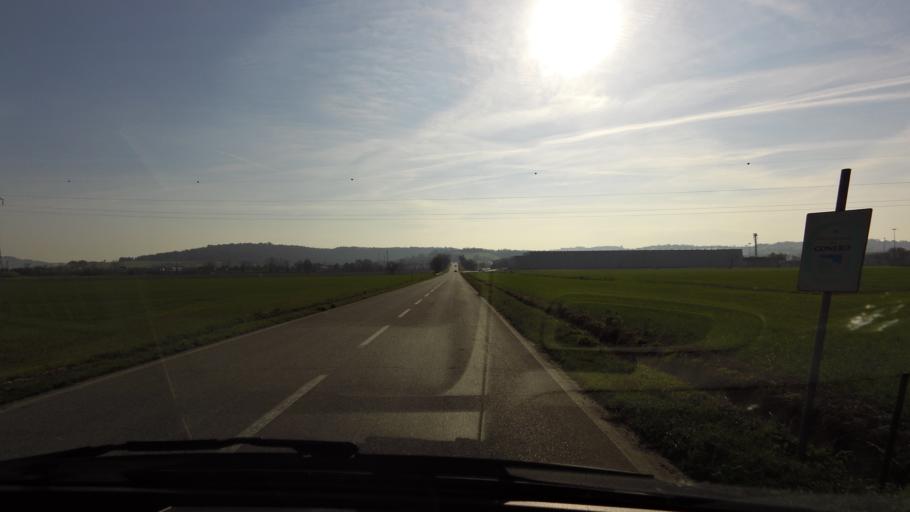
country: IT
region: The Marches
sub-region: Provincia di Ancona
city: Marcelli
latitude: 43.4823
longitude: 13.6036
